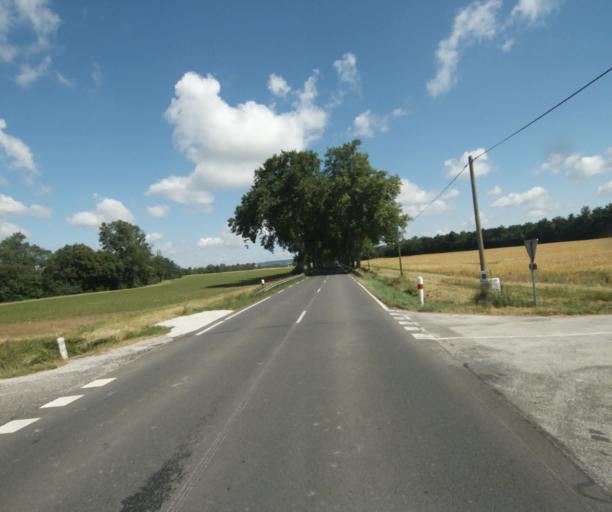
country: FR
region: Midi-Pyrenees
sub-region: Departement de la Haute-Garonne
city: Revel
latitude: 43.4349
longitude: 1.9530
